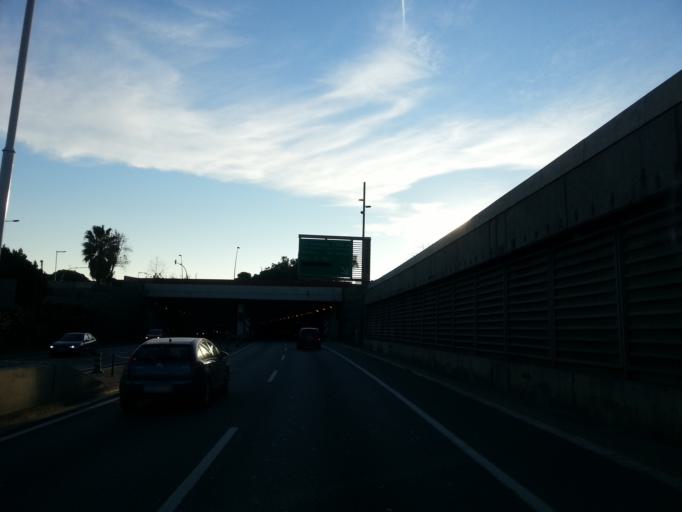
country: ES
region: Catalonia
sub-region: Provincia de Barcelona
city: Sant Marti
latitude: 41.3996
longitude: 2.2096
